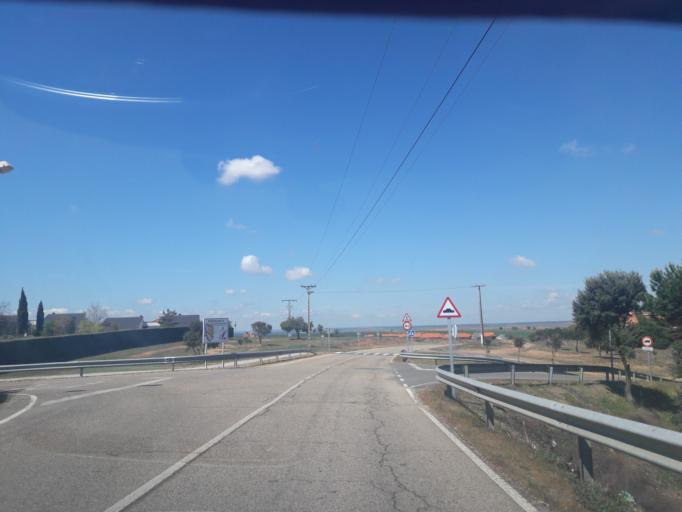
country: ES
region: Castille and Leon
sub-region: Provincia de Salamanca
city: Doninos de Salamanca
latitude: 40.9434
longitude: -5.7301
